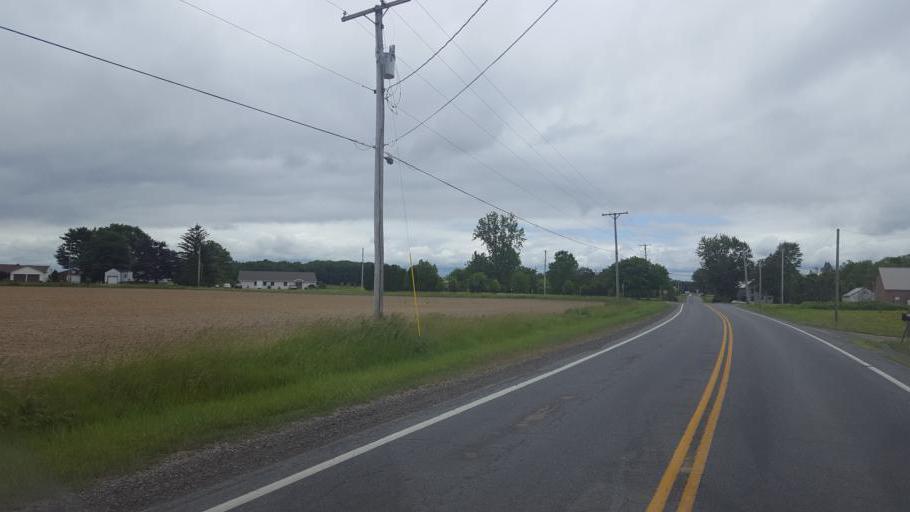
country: US
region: Ohio
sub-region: Crawford County
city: Galion
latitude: 40.7624
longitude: -82.8748
